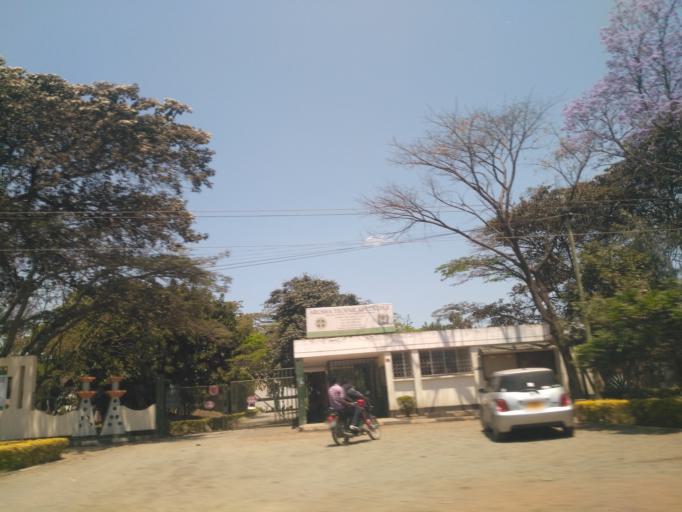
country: TZ
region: Arusha
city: Arusha
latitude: -3.3644
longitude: 36.6765
